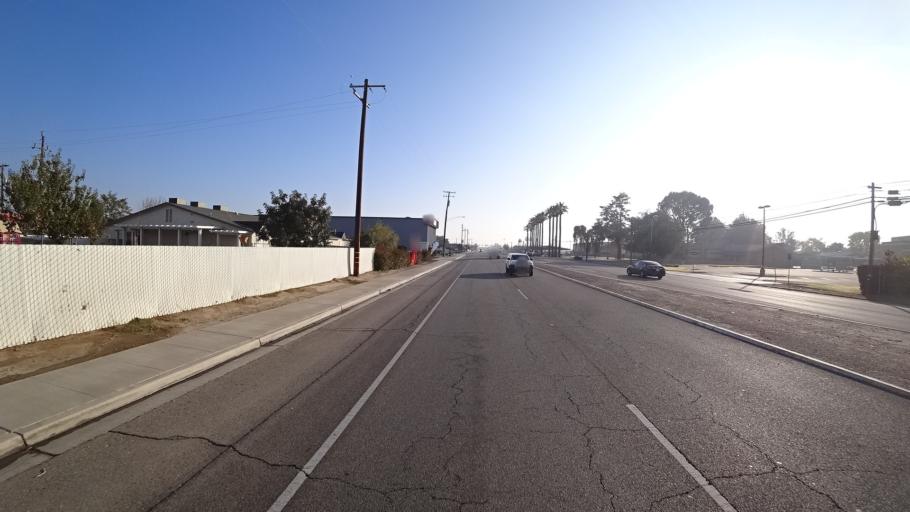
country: US
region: California
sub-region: Kern County
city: Rosedale
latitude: 35.3836
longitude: -119.1413
